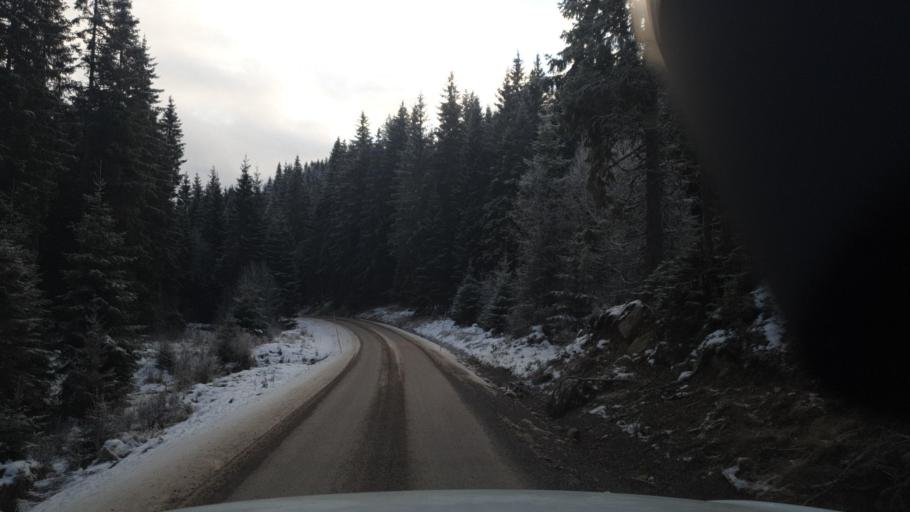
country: SE
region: Vaermland
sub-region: Eda Kommun
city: Charlottenberg
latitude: 60.0439
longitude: 12.5751
